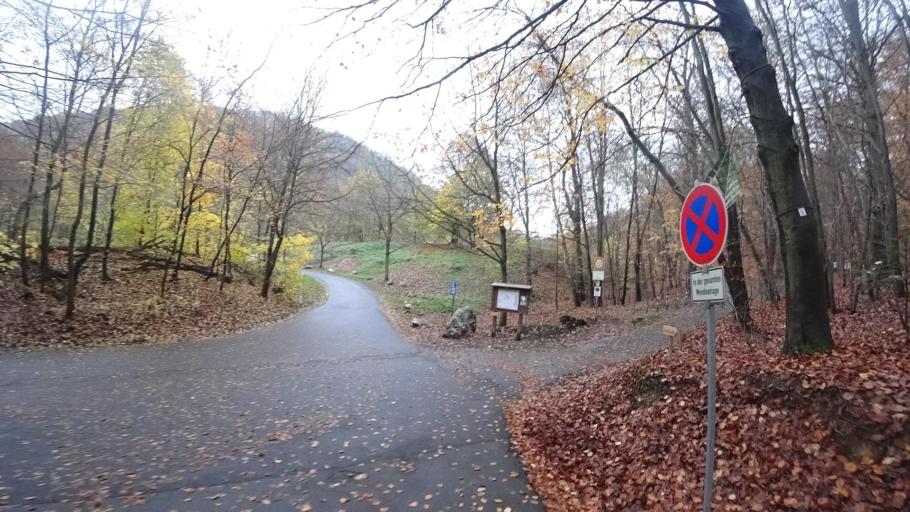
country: DE
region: Rheinland-Pfalz
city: Bad Neuenahr-Ahrweiler
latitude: 50.5306
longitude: 7.1325
